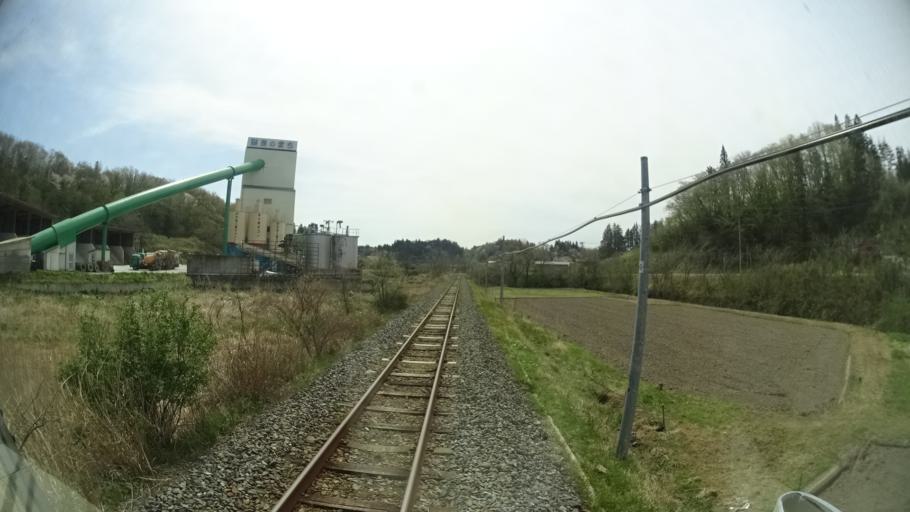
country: JP
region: Iwate
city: Ichinoseki
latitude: 38.9381
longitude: 141.3405
